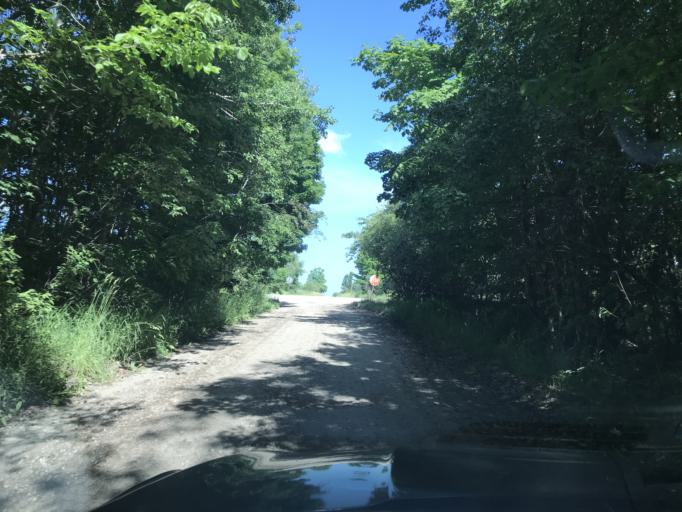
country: US
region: Michigan
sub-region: Cheboygan County
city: Cheboygan
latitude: 45.6216
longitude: -84.6722
